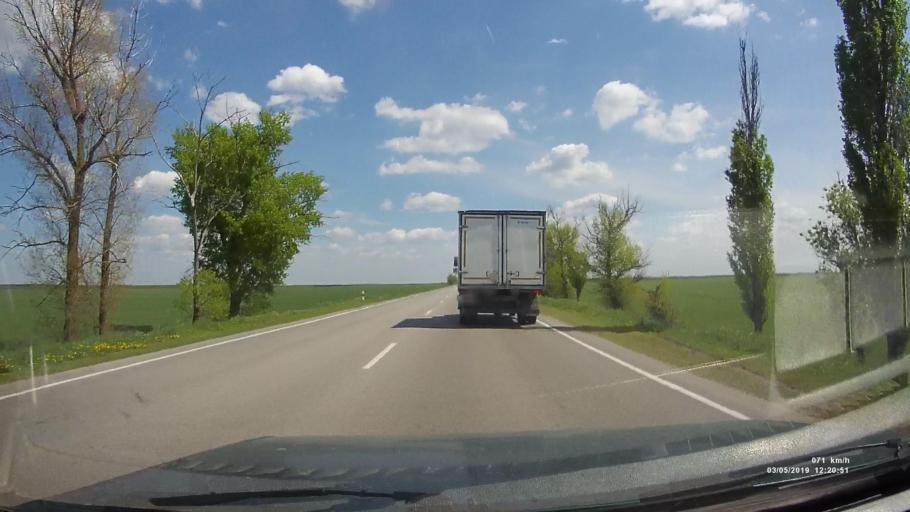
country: RU
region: Rostov
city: Melikhovskaya
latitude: 47.4049
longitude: 40.6286
